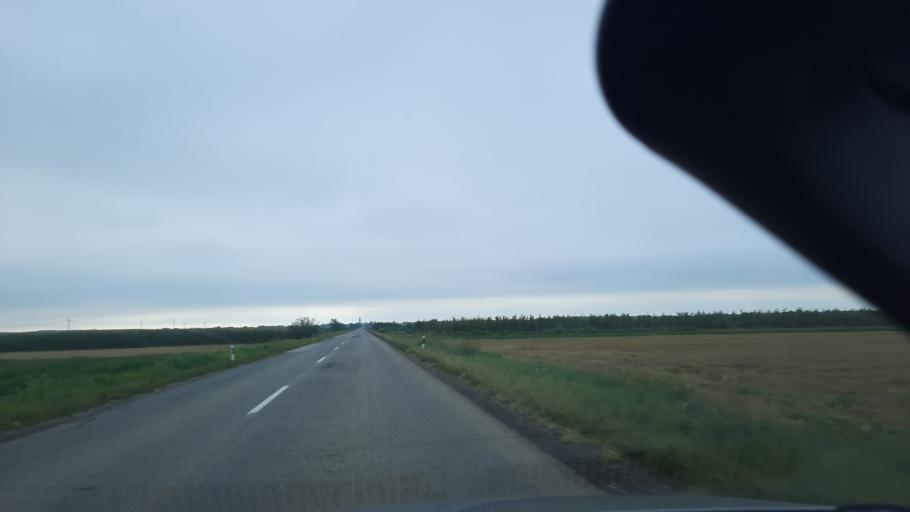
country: RS
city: Farkazdin
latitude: 45.1963
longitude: 20.4503
